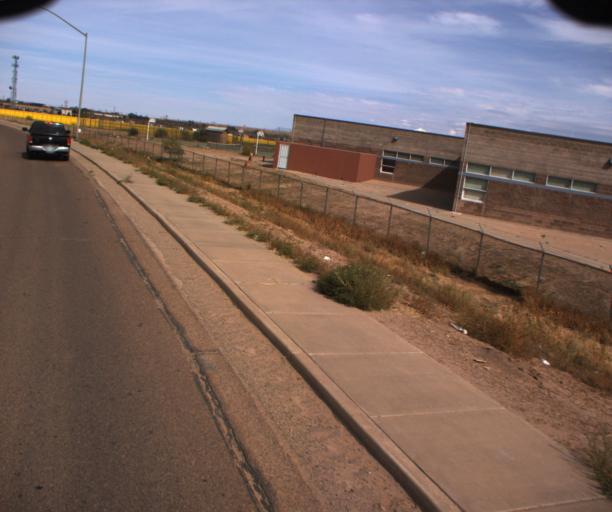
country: US
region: Arizona
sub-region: Apache County
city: Chinle
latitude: 36.1580
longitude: -109.5826
